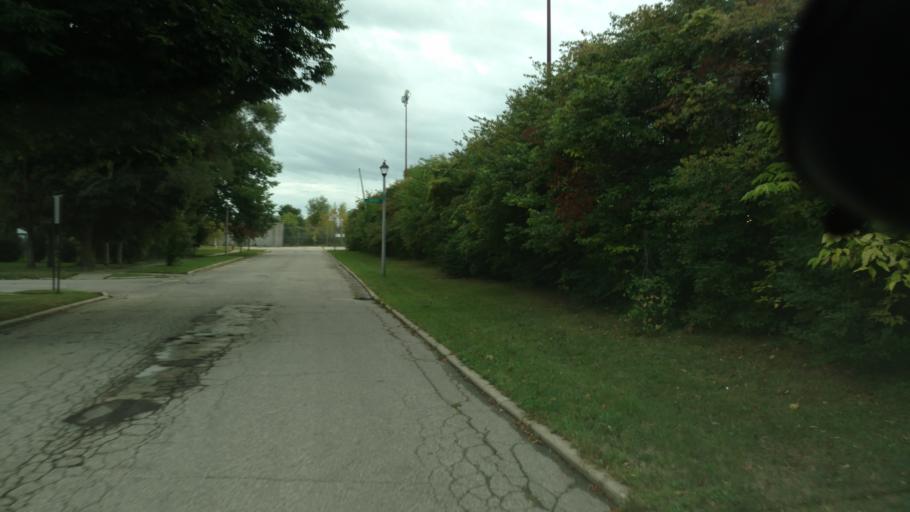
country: US
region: Michigan
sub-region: Ingham County
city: Edgemont Park
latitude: 42.7398
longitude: -84.5796
